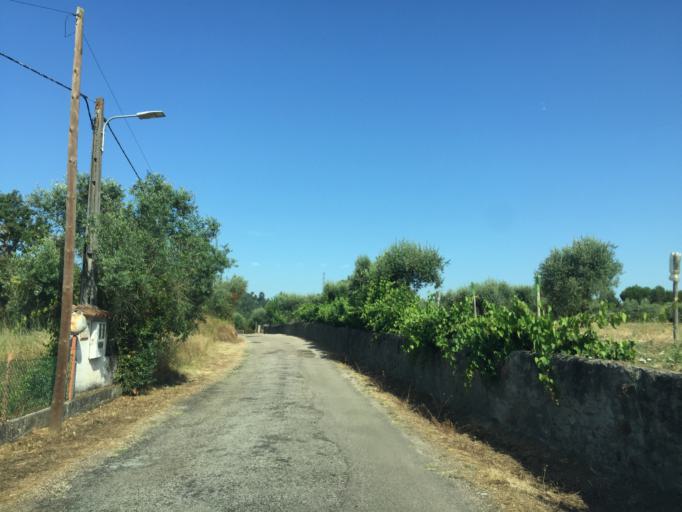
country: PT
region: Santarem
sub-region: Tomar
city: Tomar
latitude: 39.6559
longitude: -8.3749
